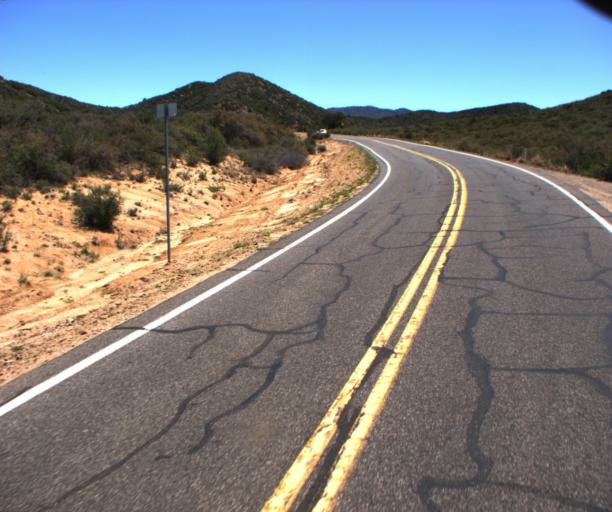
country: US
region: Arizona
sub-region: Yavapai County
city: Prescott
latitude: 34.4234
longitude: -112.5594
